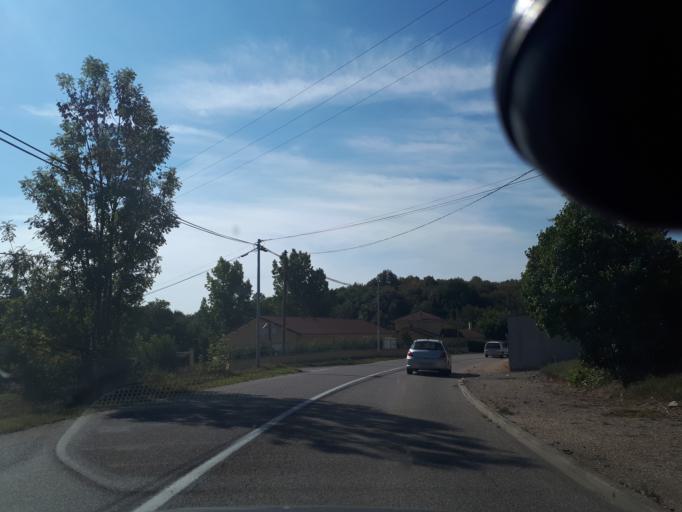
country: FR
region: Rhone-Alpes
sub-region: Departement de l'Isere
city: Chatonnay
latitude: 45.5164
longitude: 5.2111
